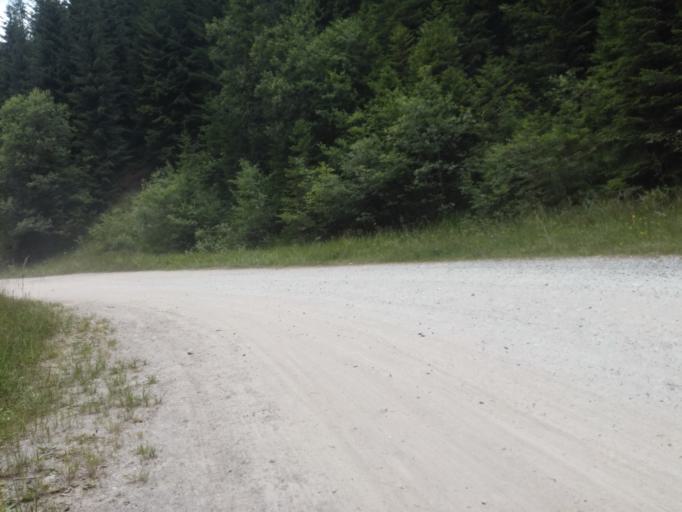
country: RO
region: Valcea
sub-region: Comuna Voineasa
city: Voineasa
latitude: 45.4336
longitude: 23.7620
